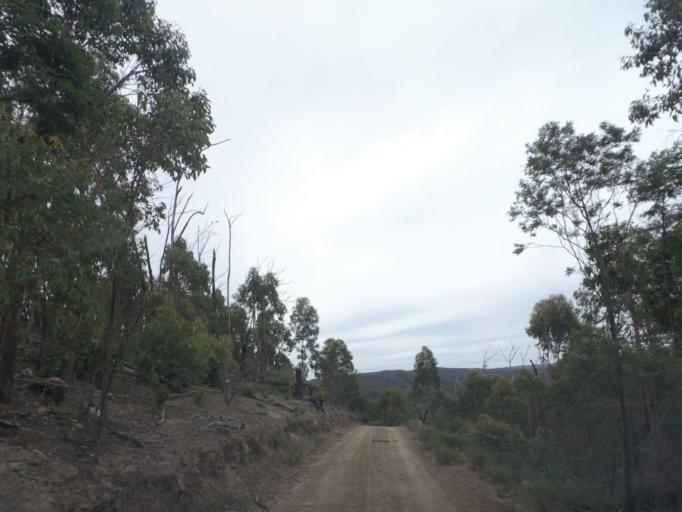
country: AU
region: Victoria
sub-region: Murrindindi
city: Alexandra
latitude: -37.3758
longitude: 145.5604
